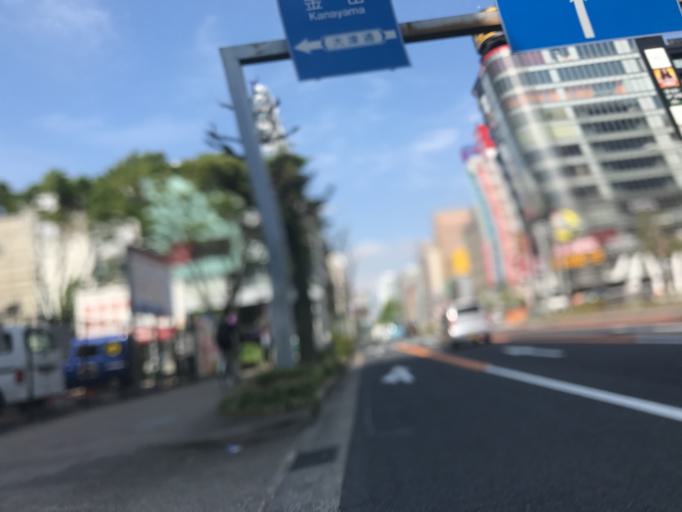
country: JP
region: Aichi
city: Nagoya-shi
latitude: 35.1698
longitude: 136.9077
